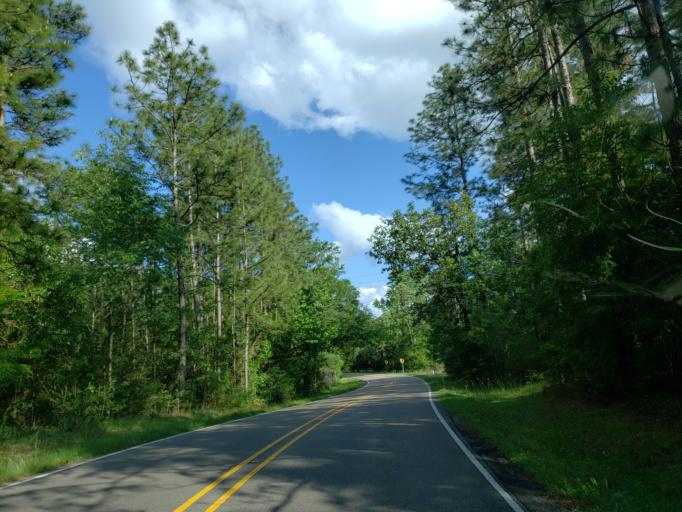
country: US
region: Mississippi
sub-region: Lamar County
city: West Hattiesburg
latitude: 31.2734
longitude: -89.3642
